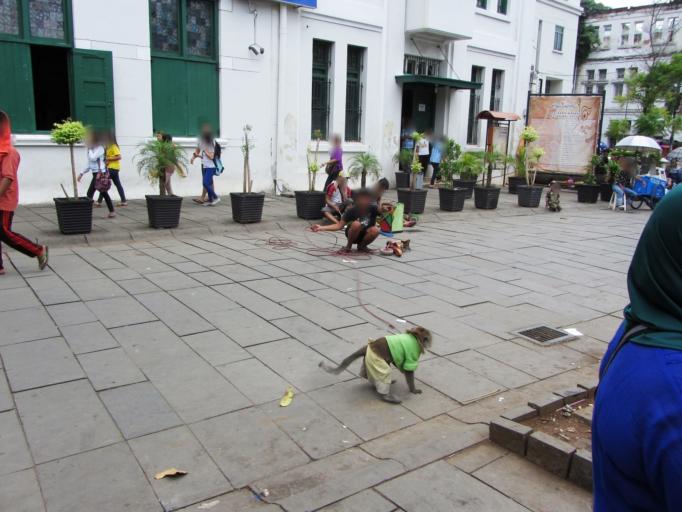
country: ID
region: Jakarta Raya
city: Jakarta
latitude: -6.1346
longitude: 106.8129
